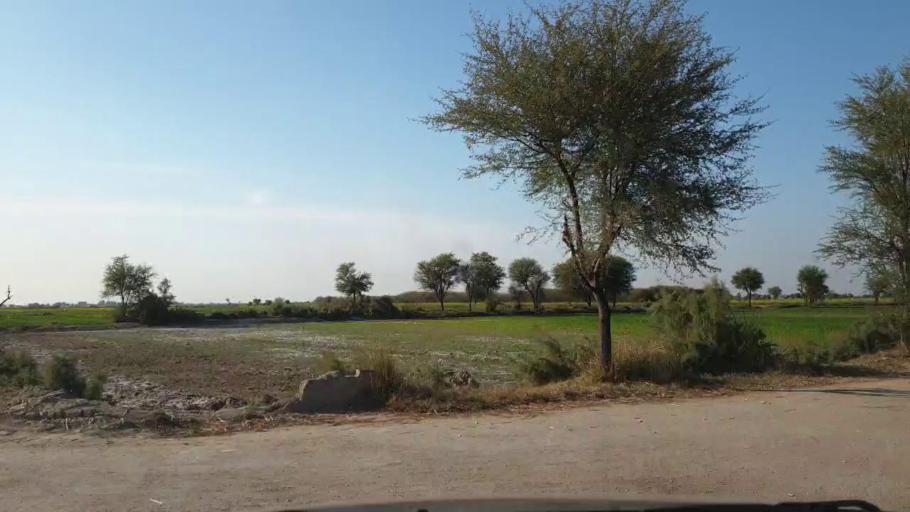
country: PK
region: Sindh
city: Khadro
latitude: 26.2034
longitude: 68.7544
